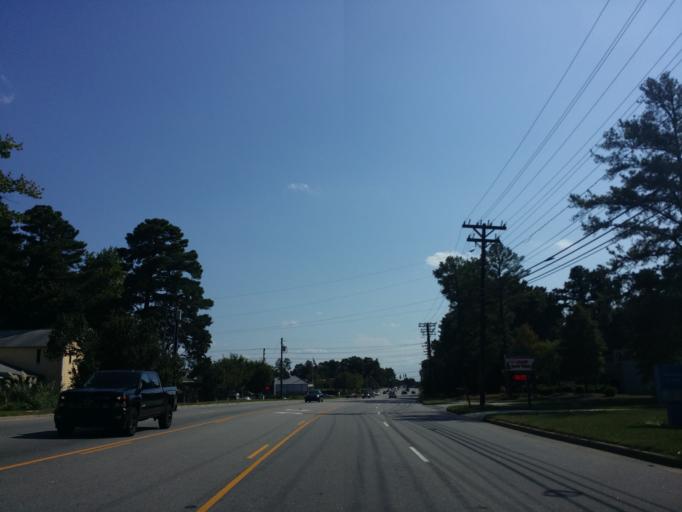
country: US
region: North Carolina
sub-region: Durham County
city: Durham
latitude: 35.9321
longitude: -78.8430
